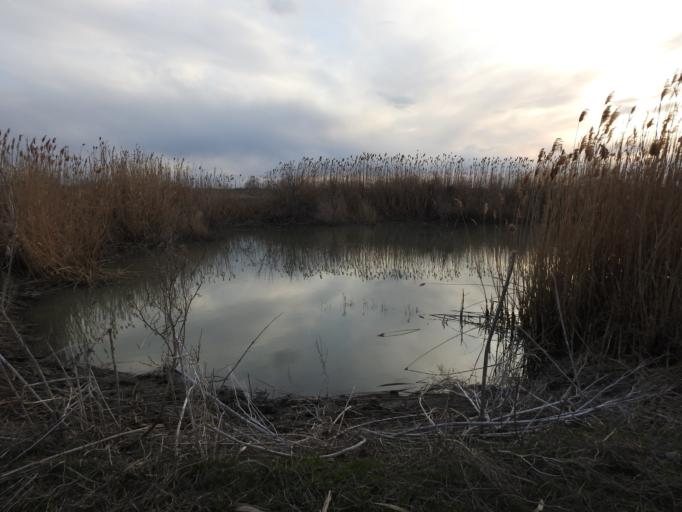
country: RU
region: Saratov
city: Engel's
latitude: 51.4223
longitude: 46.1788
